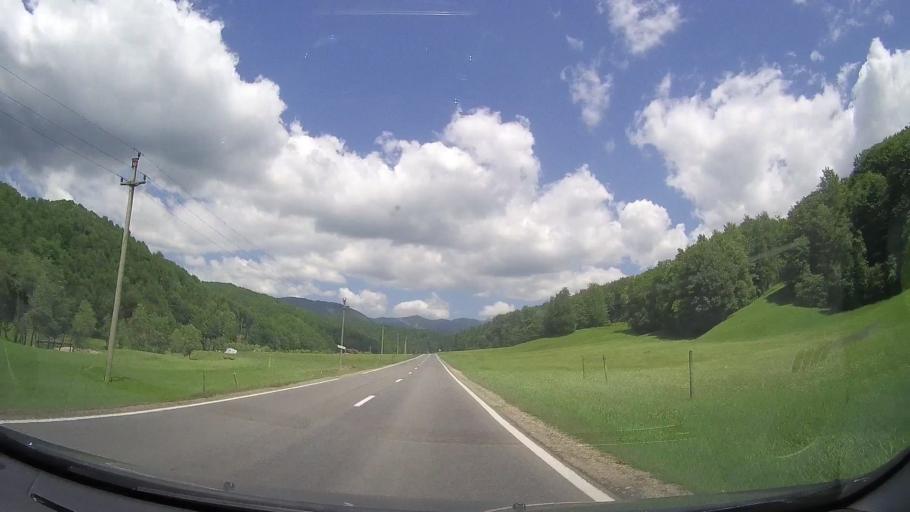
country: RO
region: Prahova
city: Maneciu
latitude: 45.4257
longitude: 25.9409
